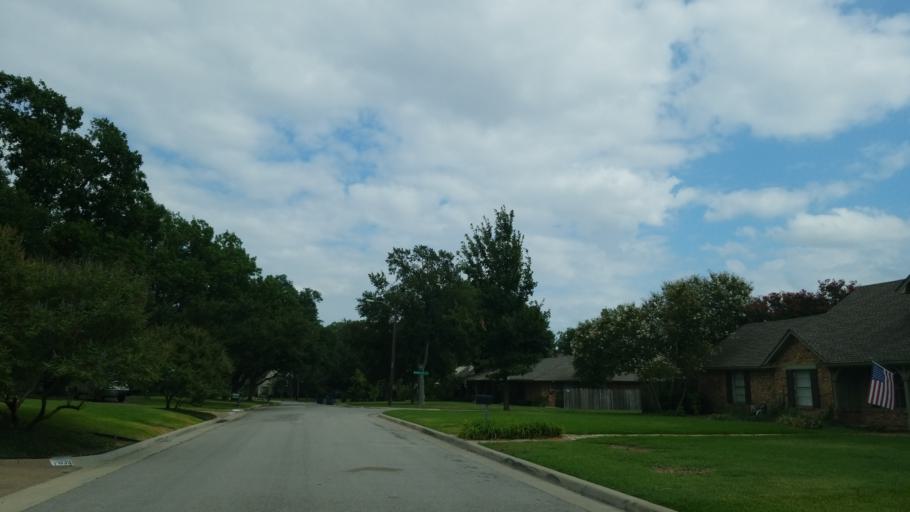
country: US
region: Texas
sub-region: Dallas County
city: Addison
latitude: 32.9420
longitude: -96.7827
